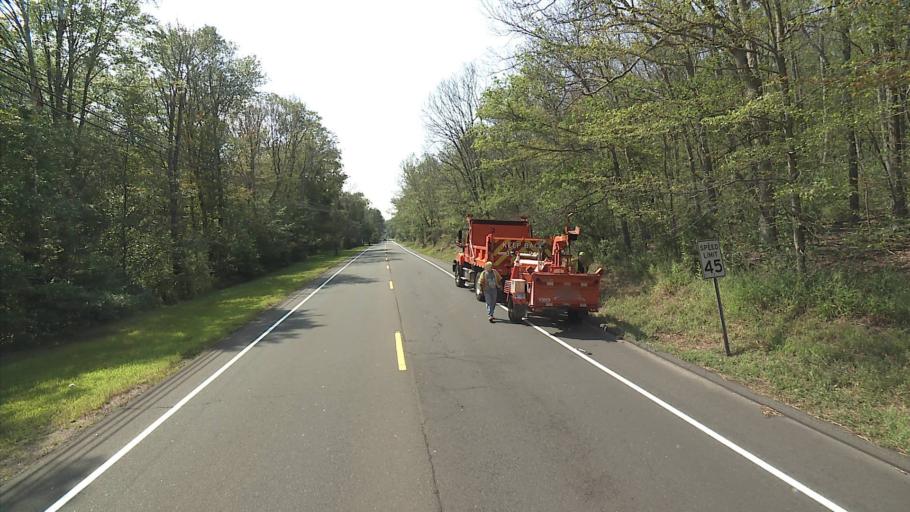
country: US
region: Connecticut
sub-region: Middlesex County
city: Durham
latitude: 41.4210
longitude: -72.6535
